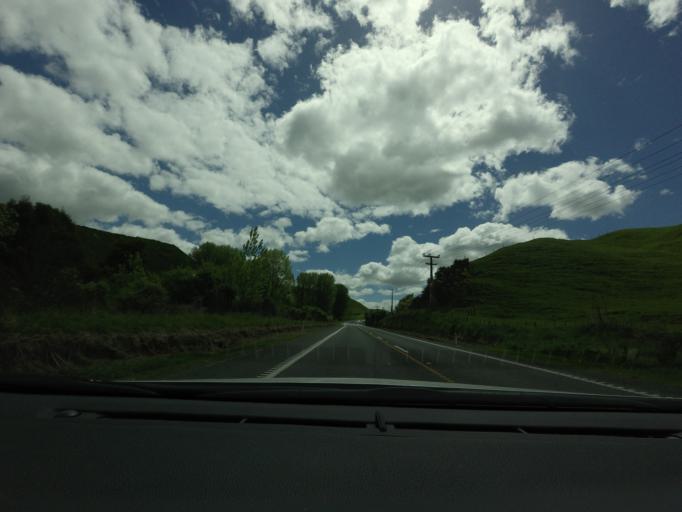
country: NZ
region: Bay of Plenty
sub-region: Rotorua District
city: Rotorua
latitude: -38.3039
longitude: 176.3689
